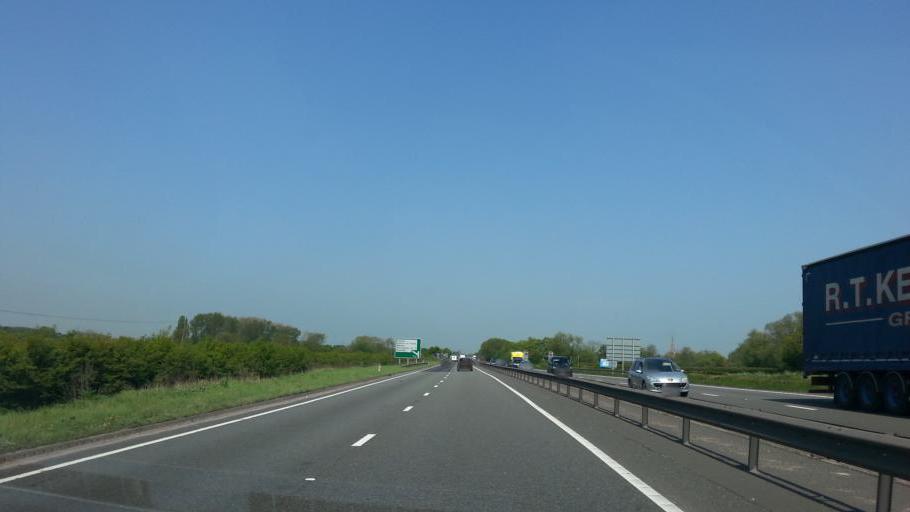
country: GB
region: England
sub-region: Nottinghamshire
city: South Collingham
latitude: 53.1567
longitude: -0.8058
